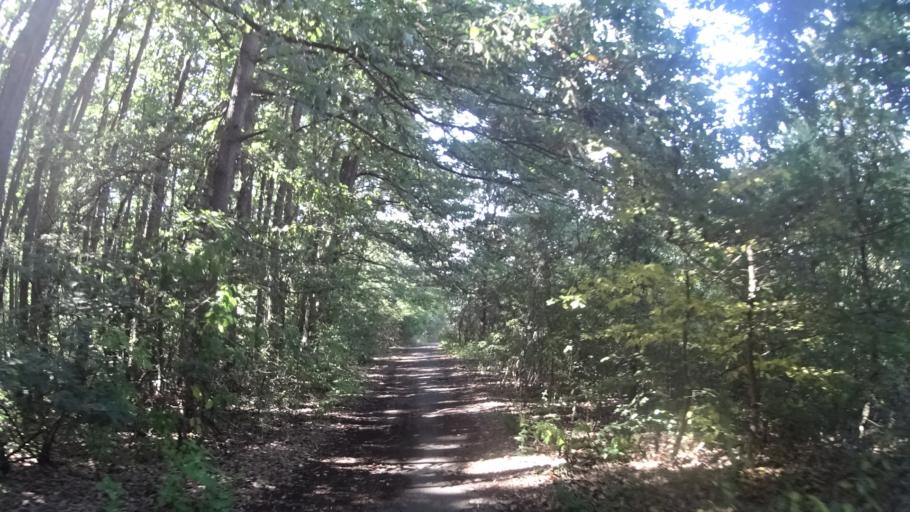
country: AT
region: Lower Austria
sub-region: Politischer Bezirk Ganserndorf
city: Angern an der March
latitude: 48.3567
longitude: 16.8809
